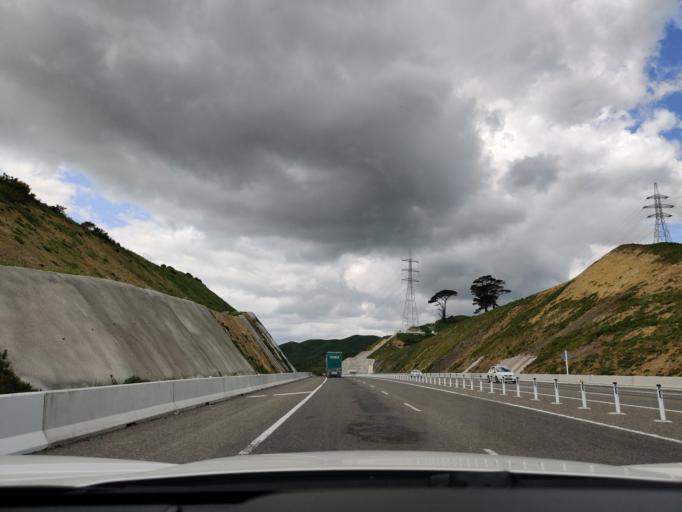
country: NZ
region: Wellington
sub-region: Porirua City
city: Porirua
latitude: -41.1550
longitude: 174.8765
